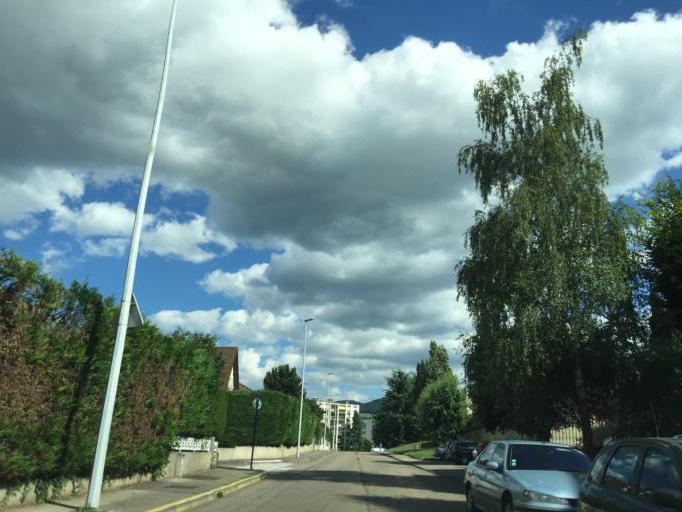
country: FR
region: Rhone-Alpes
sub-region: Departement de la Loire
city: Saint-Chamond
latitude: 45.4787
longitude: 4.5334
